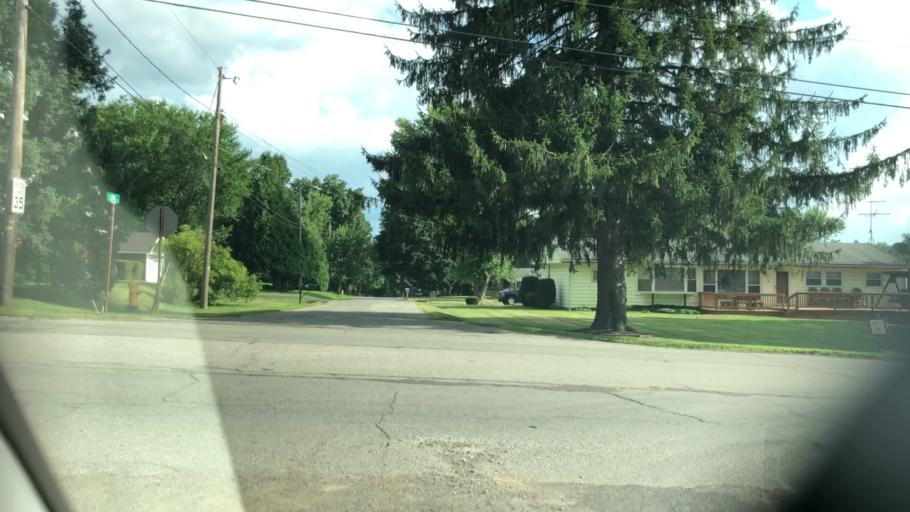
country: US
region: Ohio
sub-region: Summit County
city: Norton
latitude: 41.0259
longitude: -81.6306
